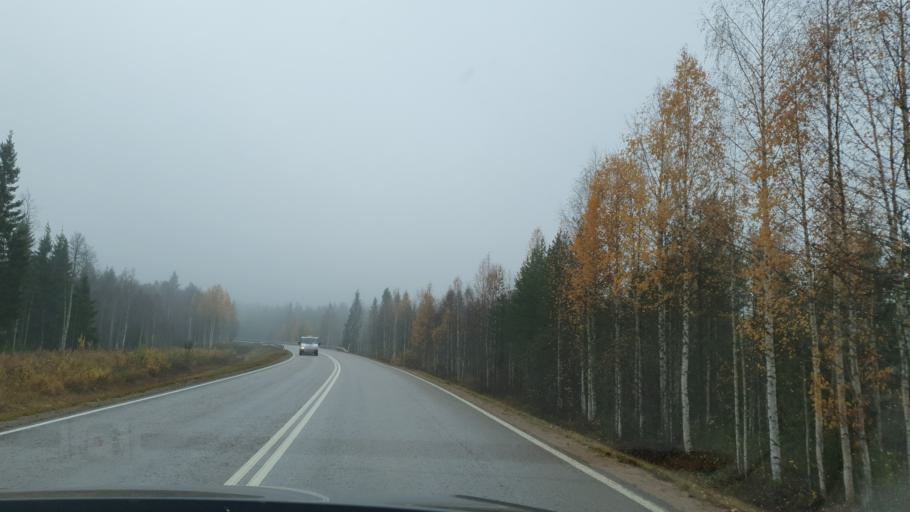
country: FI
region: Lapland
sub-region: Rovaniemi
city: Rovaniemi
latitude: 66.8172
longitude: 25.3954
